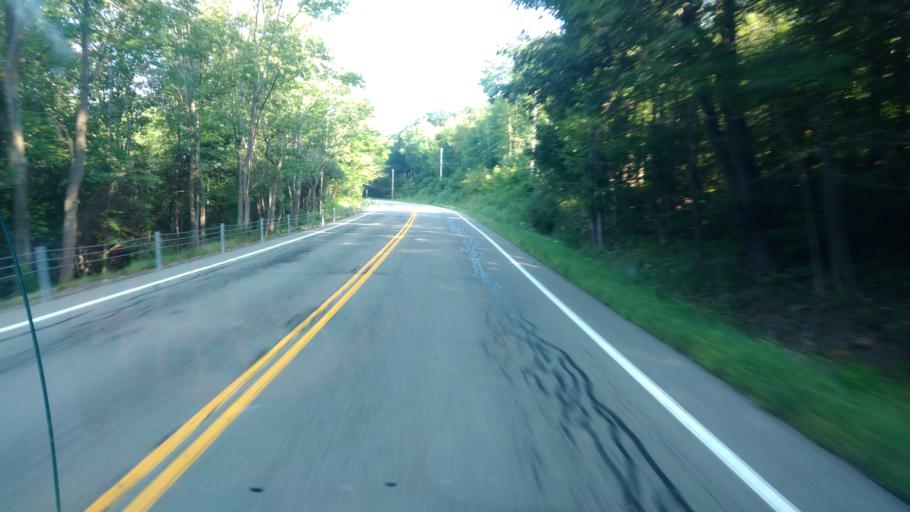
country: US
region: New York
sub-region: Allegany County
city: Andover
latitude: 42.1439
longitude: -77.6807
